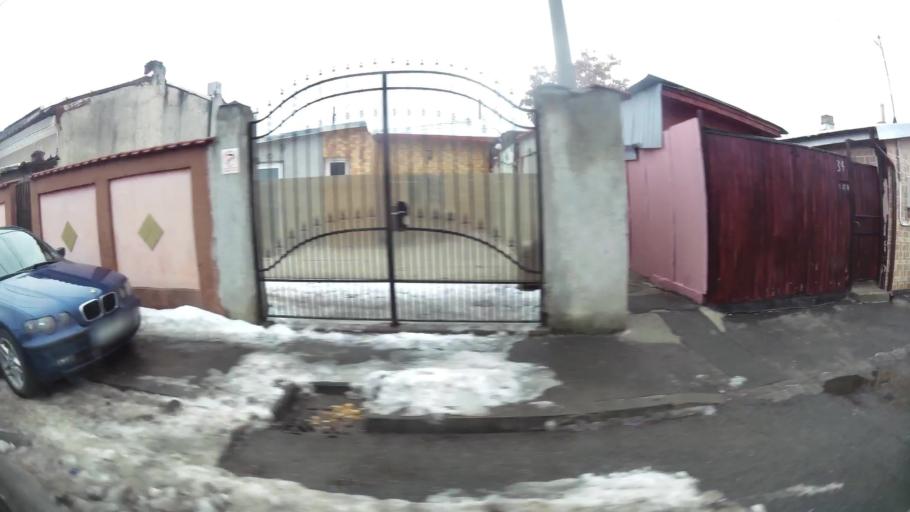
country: RO
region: Ilfov
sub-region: Comuna Popesti-Leordeni
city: Popesti-Leordeni
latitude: 44.4087
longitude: 26.1621
